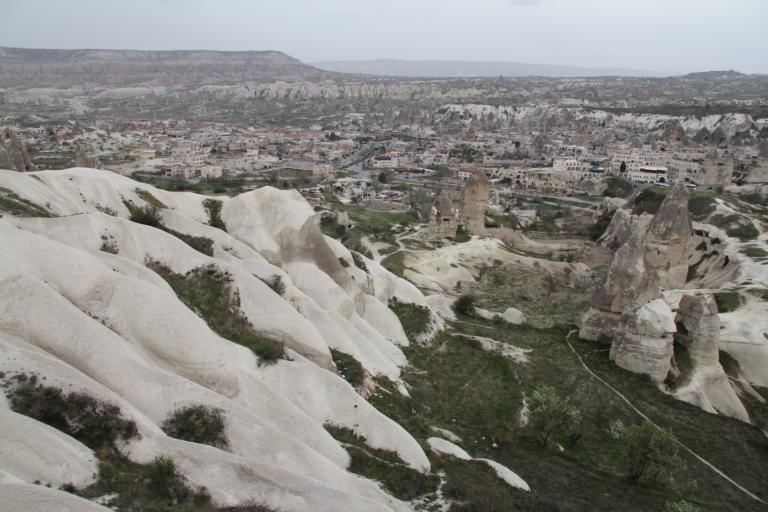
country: TR
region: Nevsehir
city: Goereme
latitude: 38.6422
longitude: 34.8193
